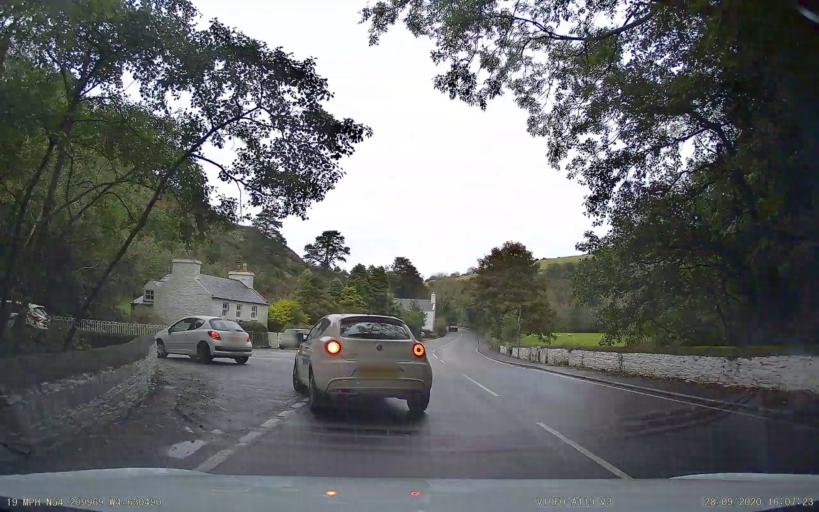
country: IM
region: Castletown
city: Castletown
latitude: 54.2100
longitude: -4.6305
